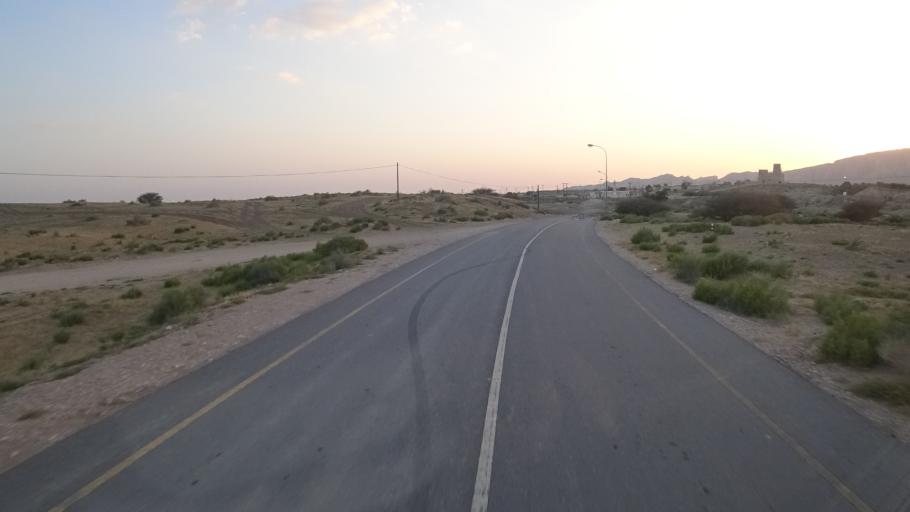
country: AE
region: Abu Dhabi
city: Al Ain
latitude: 23.9826
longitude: 55.8405
